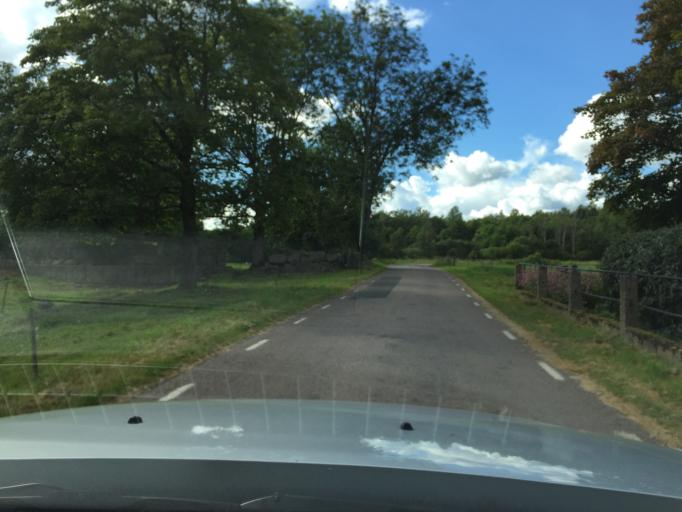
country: SE
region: Skane
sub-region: Hassleholms Kommun
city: Vinslov
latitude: 55.9743
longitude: 13.8457
